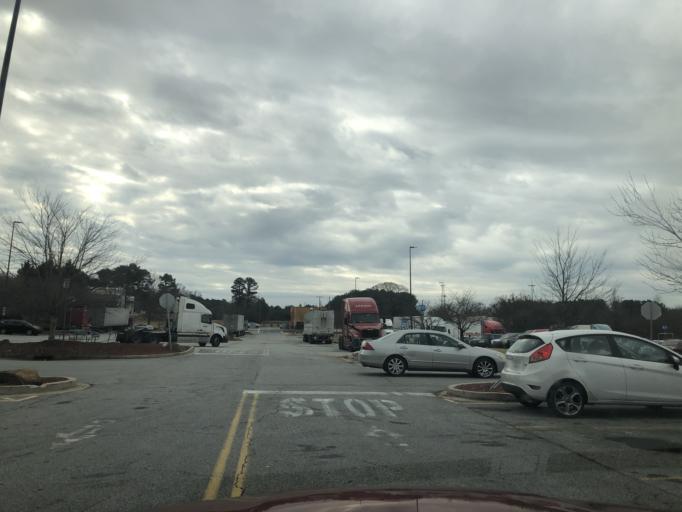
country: US
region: Georgia
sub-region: Clayton County
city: Conley
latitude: 33.6359
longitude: -84.2916
